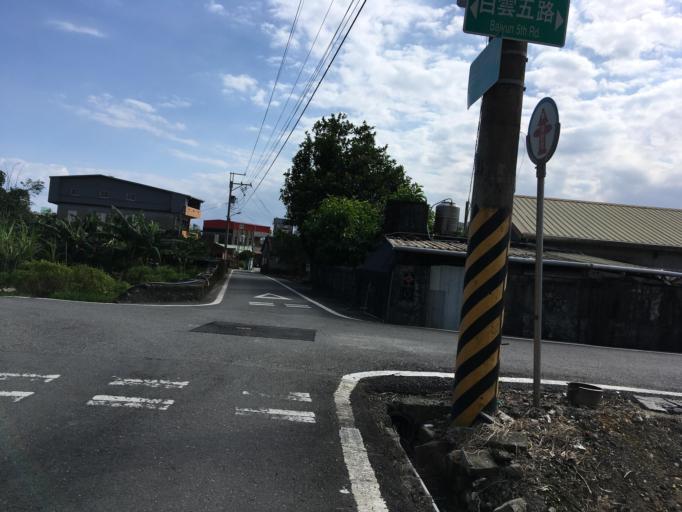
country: TW
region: Taiwan
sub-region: Yilan
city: Yilan
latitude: 24.8385
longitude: 121.7831
